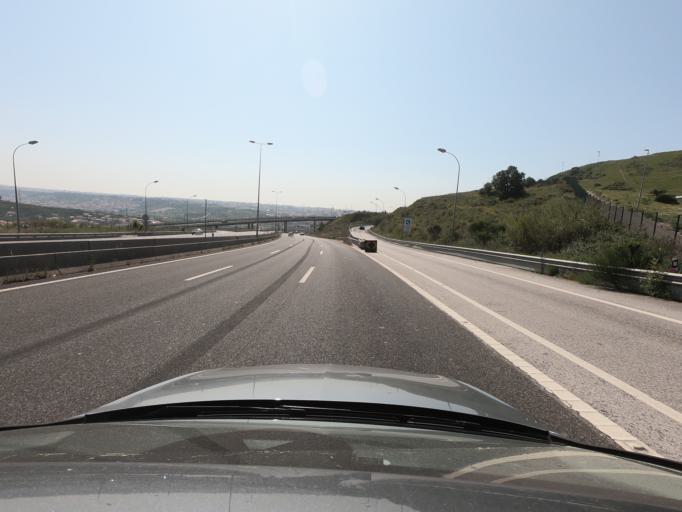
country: PT
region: Lisbon
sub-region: Odivelas
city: Famoes
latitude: 38.7761
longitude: -9.2260
